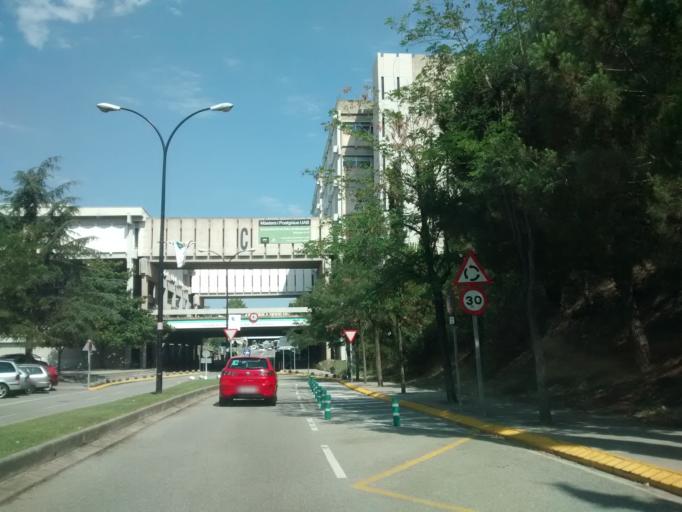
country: ES
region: Catalonia
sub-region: Provincia de Barcelona
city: Barbera del Valles
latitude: 41.4999
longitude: 2.1089
